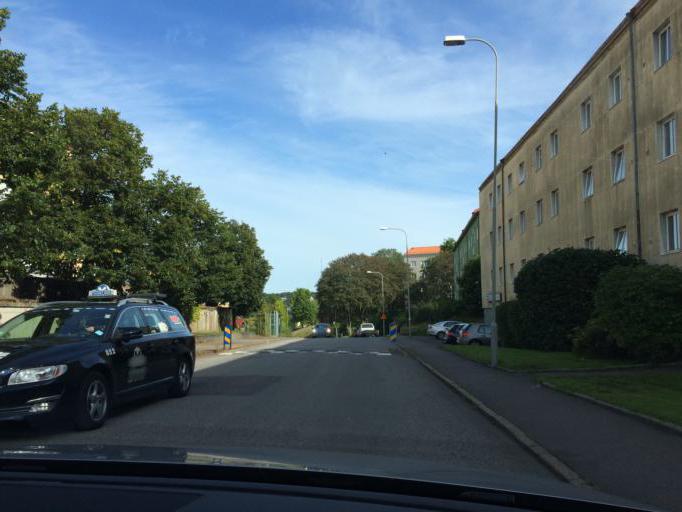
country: SE
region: Vaestra Goetaland
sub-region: Goteborg
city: Goeteborg
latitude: 57.6831
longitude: 11.9911
